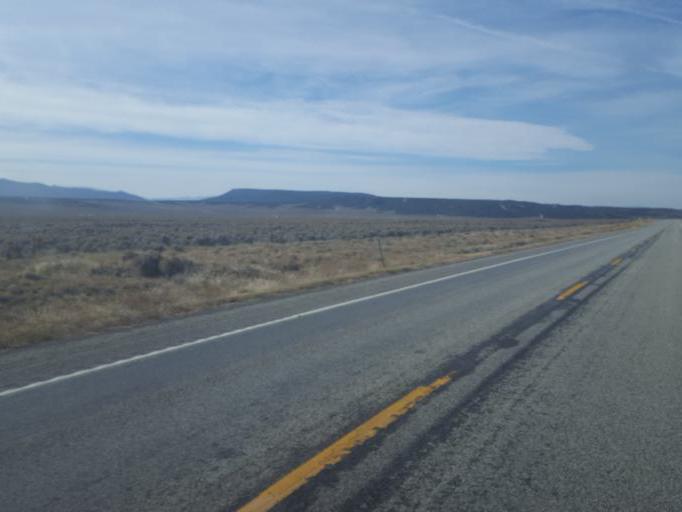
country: US
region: Colorado
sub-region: Costilla County
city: San Luis
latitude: 37.4534
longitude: -105.3675
